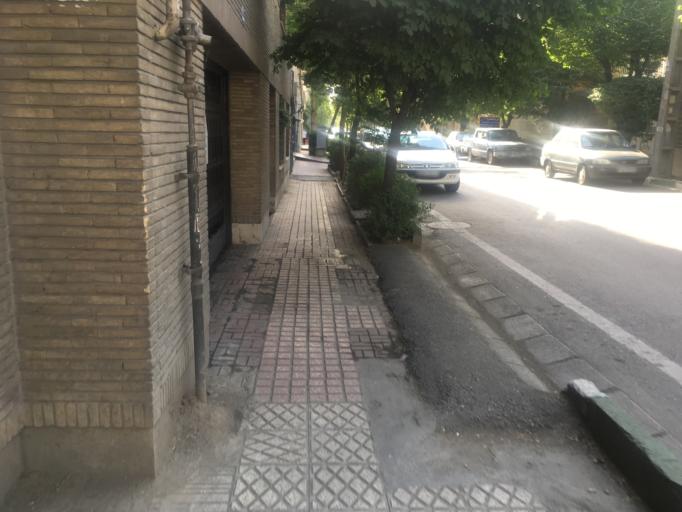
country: IR
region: Tehran
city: Tajrish
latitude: 35.7962
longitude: 51.4749
